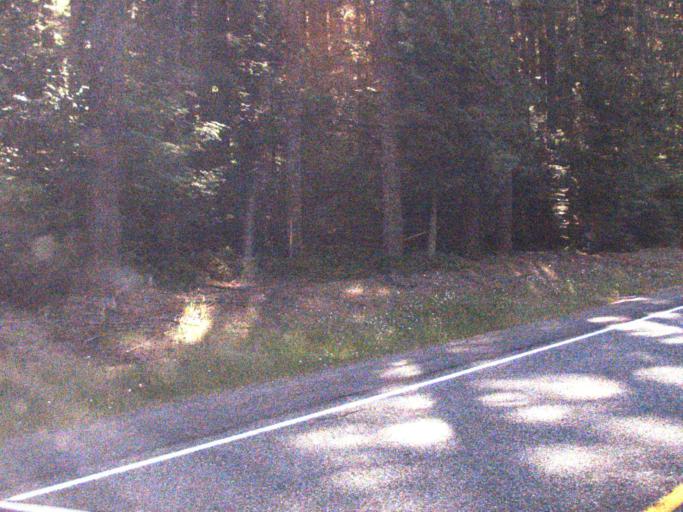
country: US
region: Washington
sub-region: King County
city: Enumclaw
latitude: 47.0363
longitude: -121.5628
